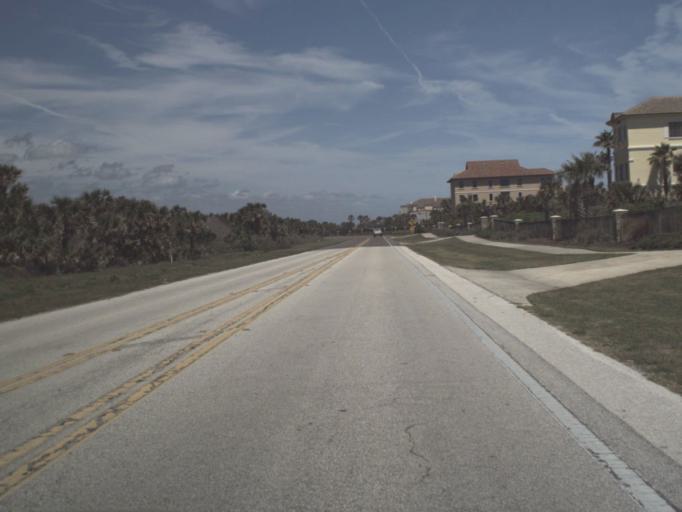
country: US
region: Florida
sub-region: Flagler County
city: Palm Coast
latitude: 29.5580
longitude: -81.1659
